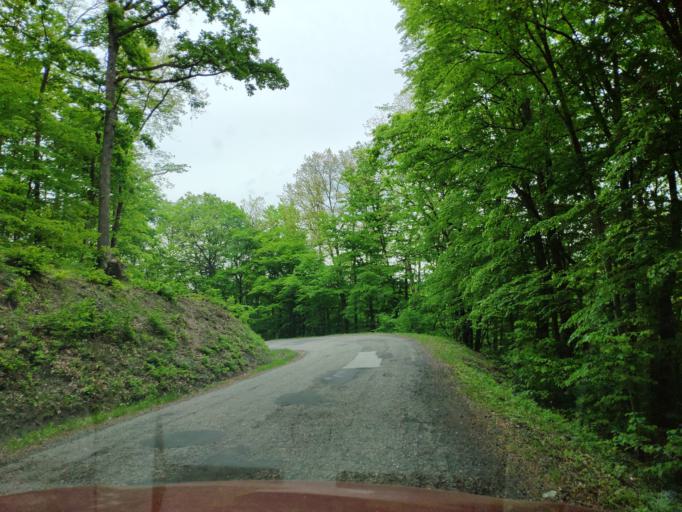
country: SK
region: Banskobystricky
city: Rimavska Sobota
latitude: 48.5093
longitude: 20.1031
